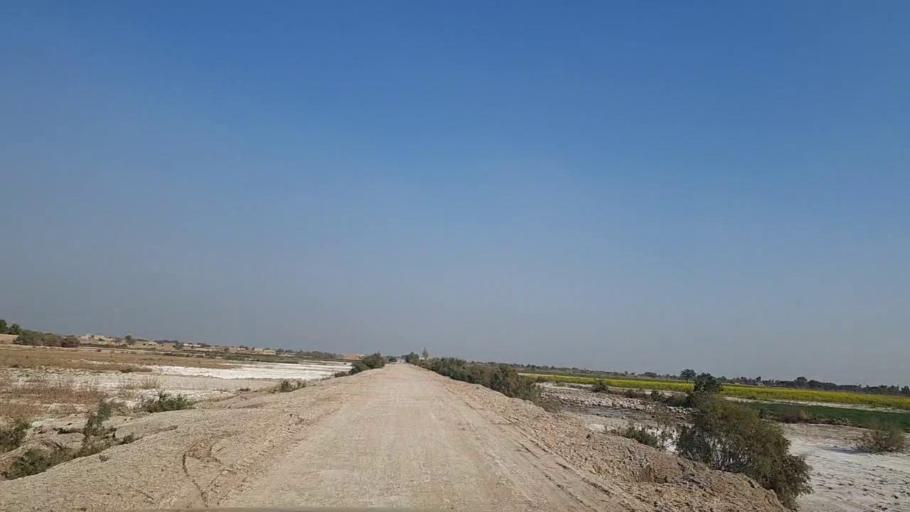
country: PK
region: Sindh
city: Daur
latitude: 26.3178
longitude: 68.1842
